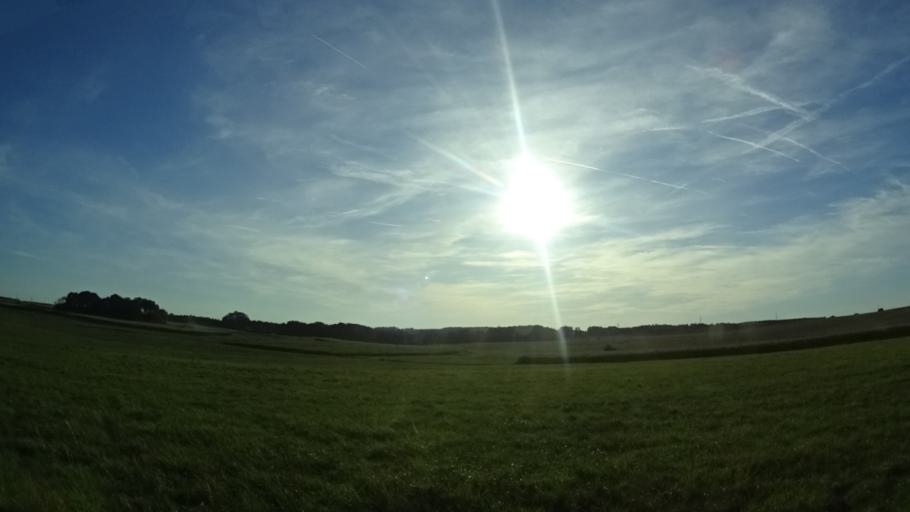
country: DE
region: Hesse
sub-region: Regierungsbezirk Darmstadt
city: Wachtersbach
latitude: 50.2996
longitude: 9.2674
